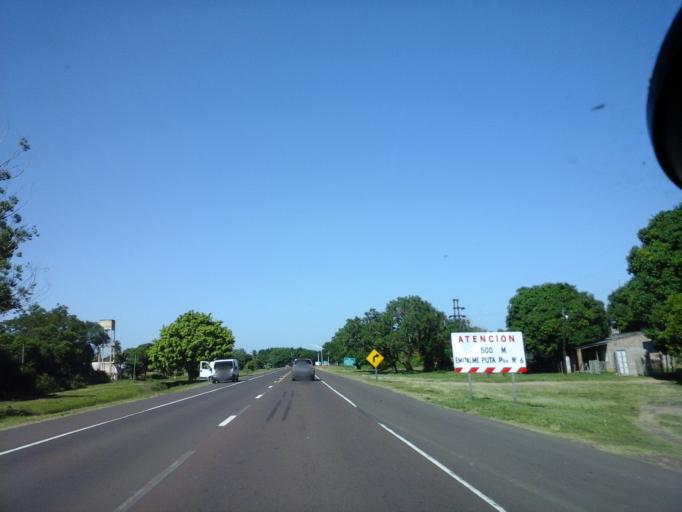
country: AR
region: Corrientes
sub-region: Departamento de San Cosme
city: San Cosme
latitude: -27.3889
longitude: -58.5489
